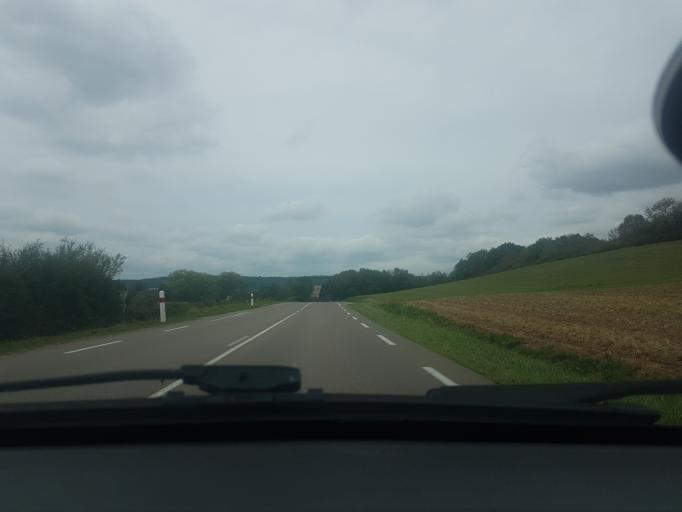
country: FR
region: Bourgogne
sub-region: Departement de la Cote-d'Or
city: Arnay-le-Duc
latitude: 47.1385
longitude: 4.4644
